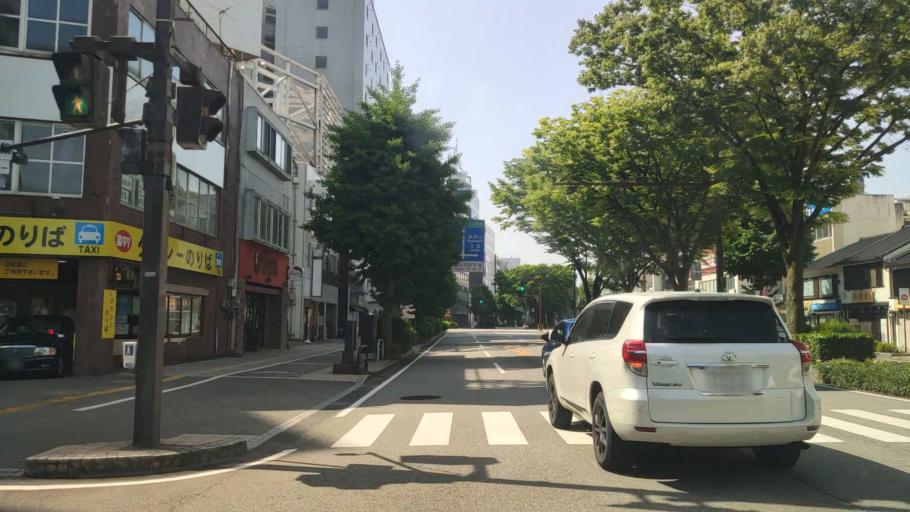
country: JP
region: Toyama
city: Toyama-shi
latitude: 36.6989
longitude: 137.2132
